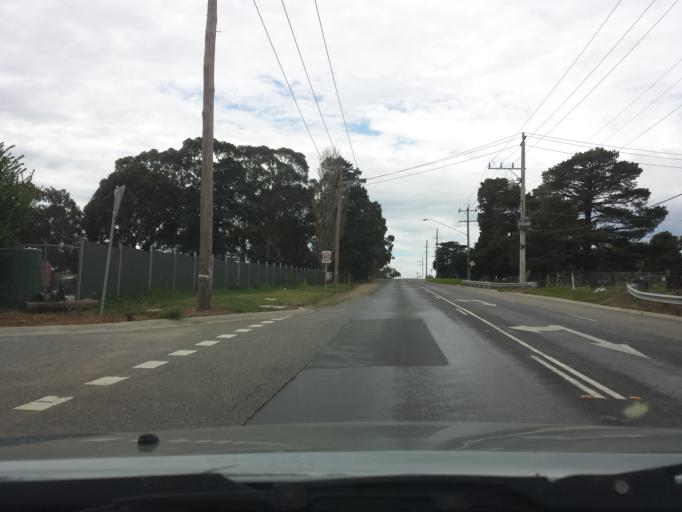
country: AU
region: Victoria
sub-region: Casey
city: Narre Warren North
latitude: -37.9807
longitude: 145.3040
